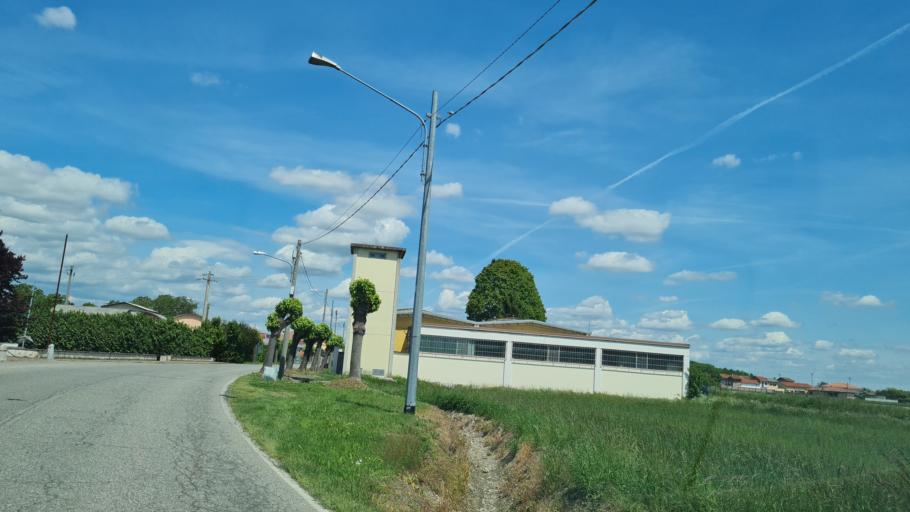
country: IT
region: Piedmont
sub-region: Provincia di Novara
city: Sillavengo
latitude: 45.5170
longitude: 8.4401
